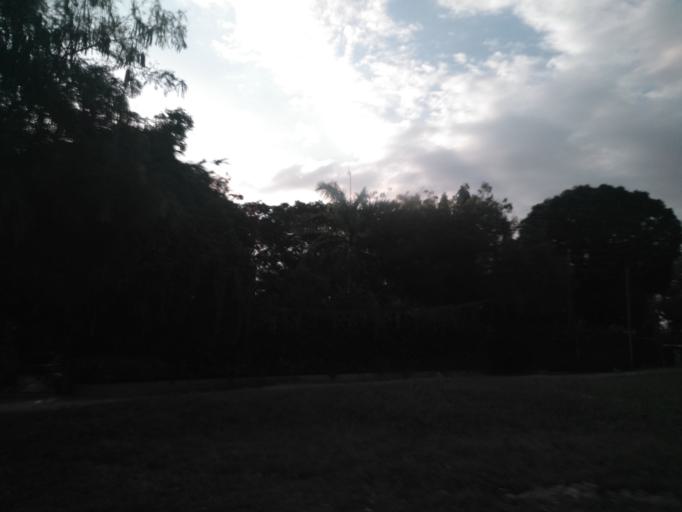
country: TZ
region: Dar es Salaam
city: Magomeni
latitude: -6.7837
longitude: 39.2723
